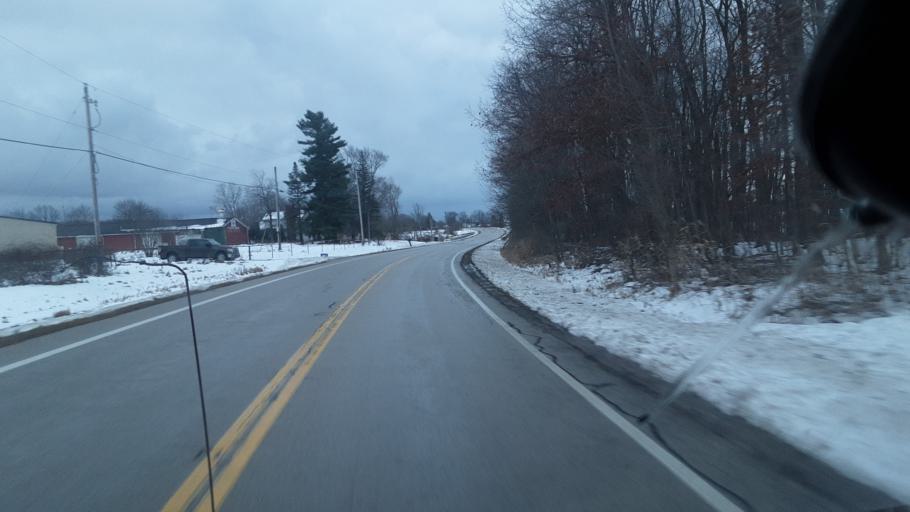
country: US
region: Ohio
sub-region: Ashtabula County
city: Jefferson
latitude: 41.7005
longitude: -80.7058
